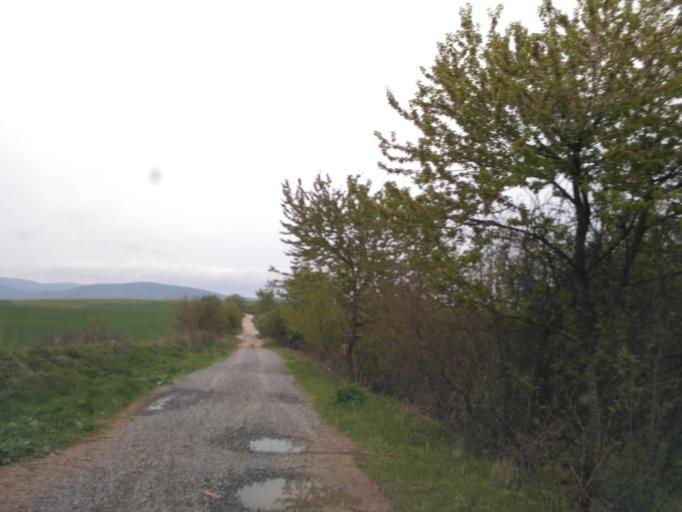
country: SK
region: Kosicky
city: Moldava nad Bodvou
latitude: 48.6655
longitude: 21.0045
